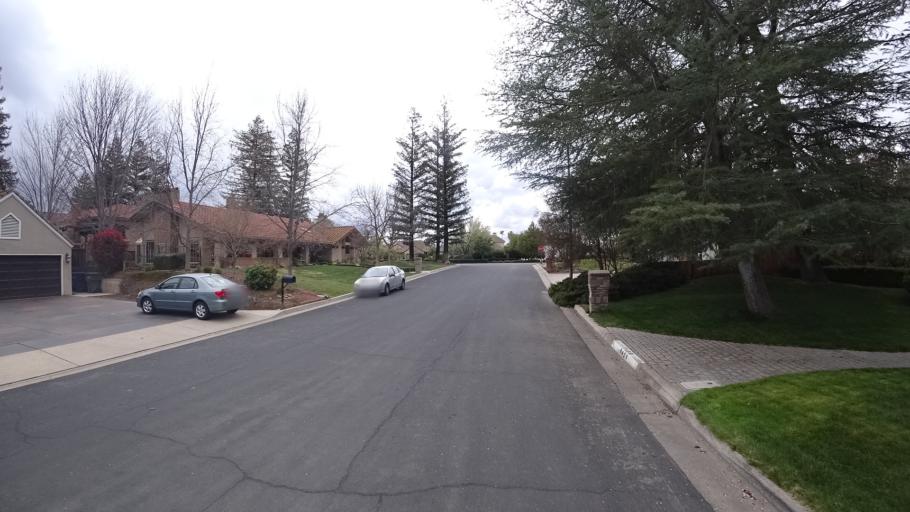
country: US
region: California
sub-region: Fresno County
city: Fresno
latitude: 36.8450
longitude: -119.8390
